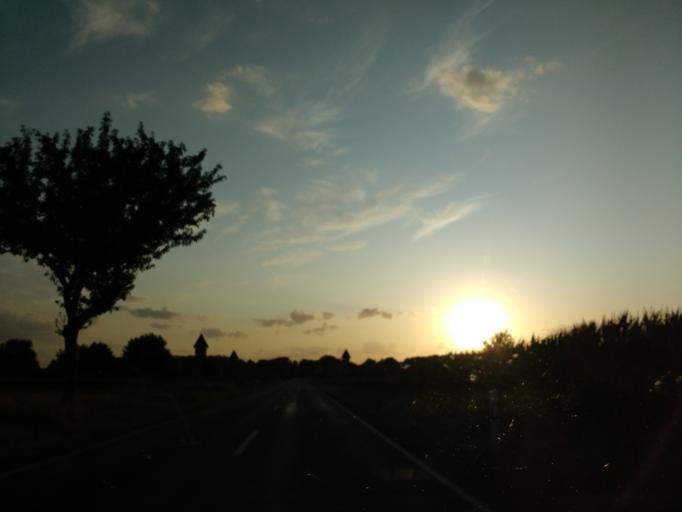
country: DE
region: Lower Saxony
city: Linsburg
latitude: 52.5341
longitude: 9.3419
